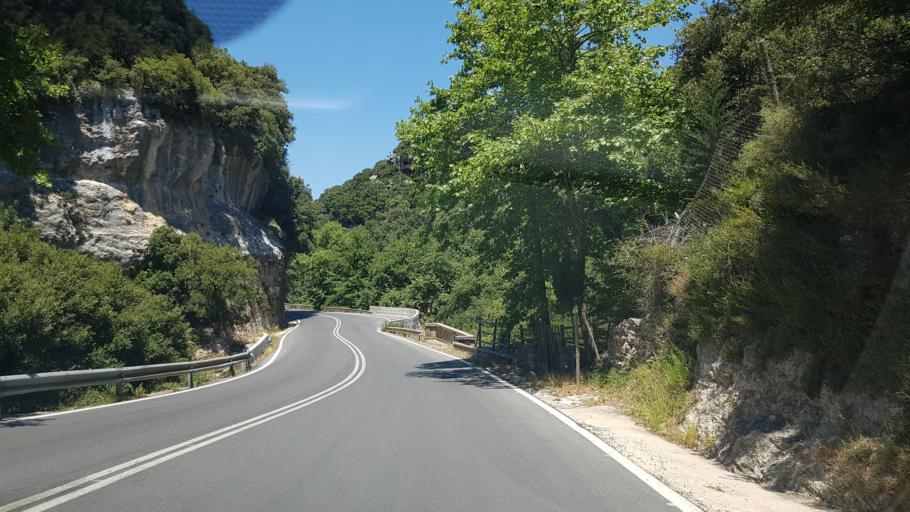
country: GR
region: Crete
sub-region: Nomos Rethymnis
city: Agia Foteini
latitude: 35.3104
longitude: 24.6269
